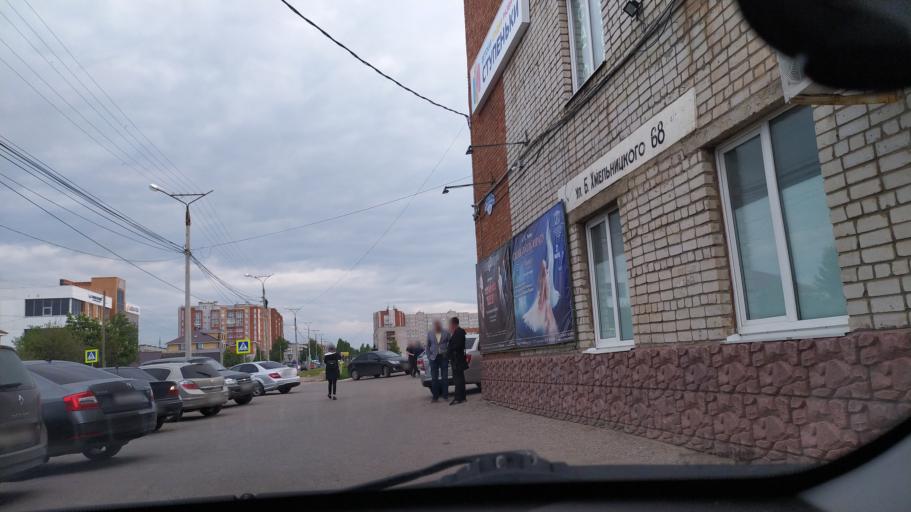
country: RU
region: Chuvashia
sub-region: Cheboksarskiy Rayon
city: Cheboksary
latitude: 56.1184
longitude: 47.2241
